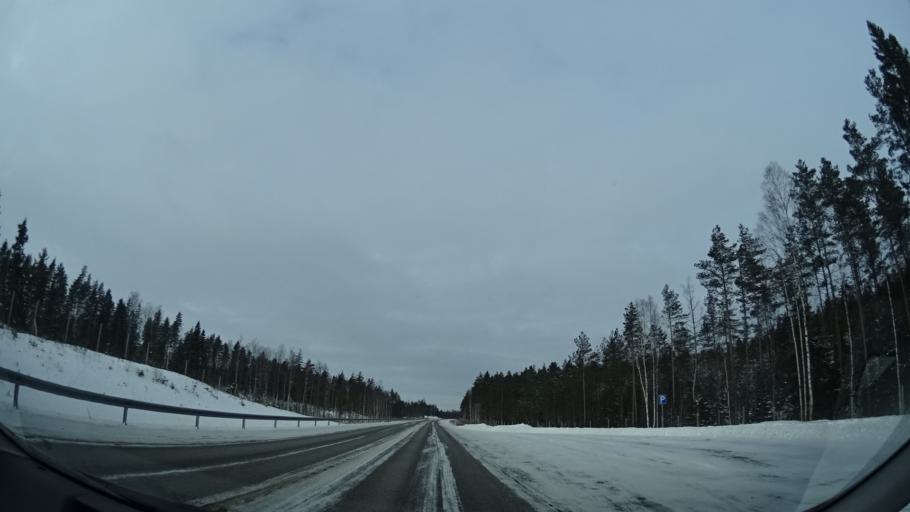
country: FI
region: Uusimaa
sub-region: Helsinki
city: Kaerkoelae
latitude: 60.6098
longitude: 24.0476
